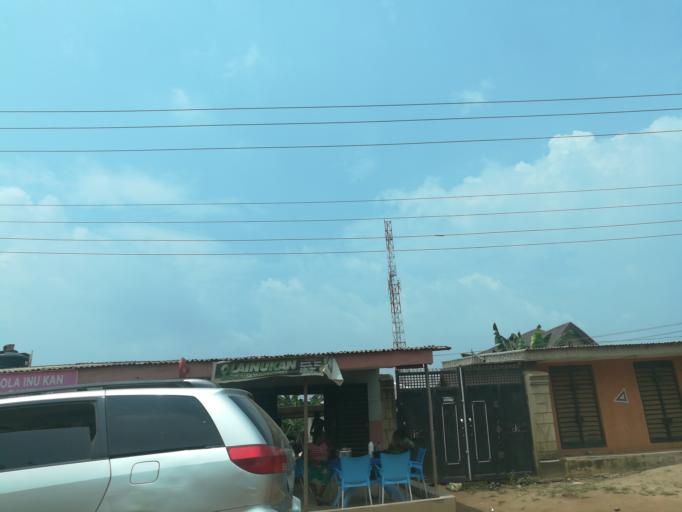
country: NG
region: Lagos
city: Ikorodu
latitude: 6.6043
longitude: 3.6024
